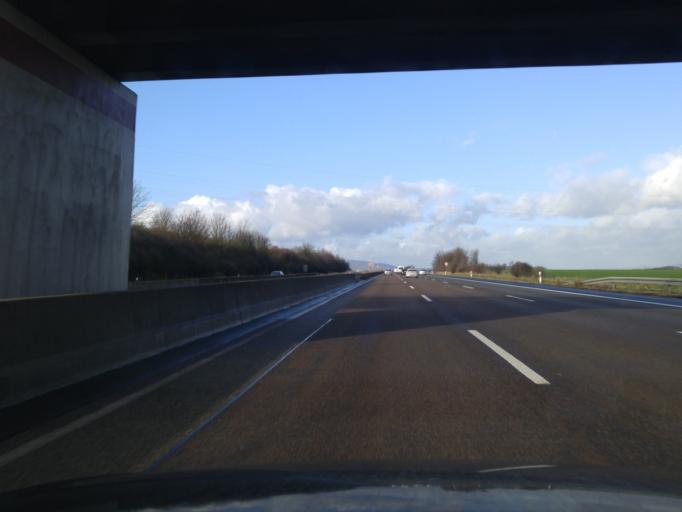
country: DE
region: Hesse
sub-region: Regierungsbezirk Kassel
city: Guxhagen
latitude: 51.1891
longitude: 9.4721
